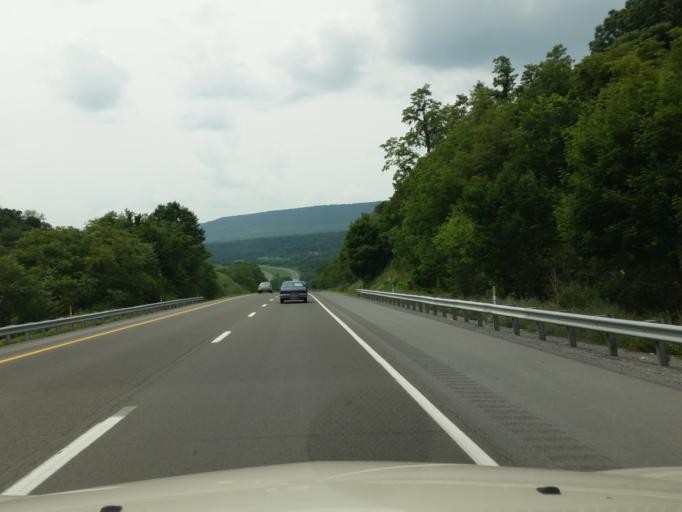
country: US
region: Pennsylvania
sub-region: Juniata County
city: Mifflintown
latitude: 40.5960
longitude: -77.3801
